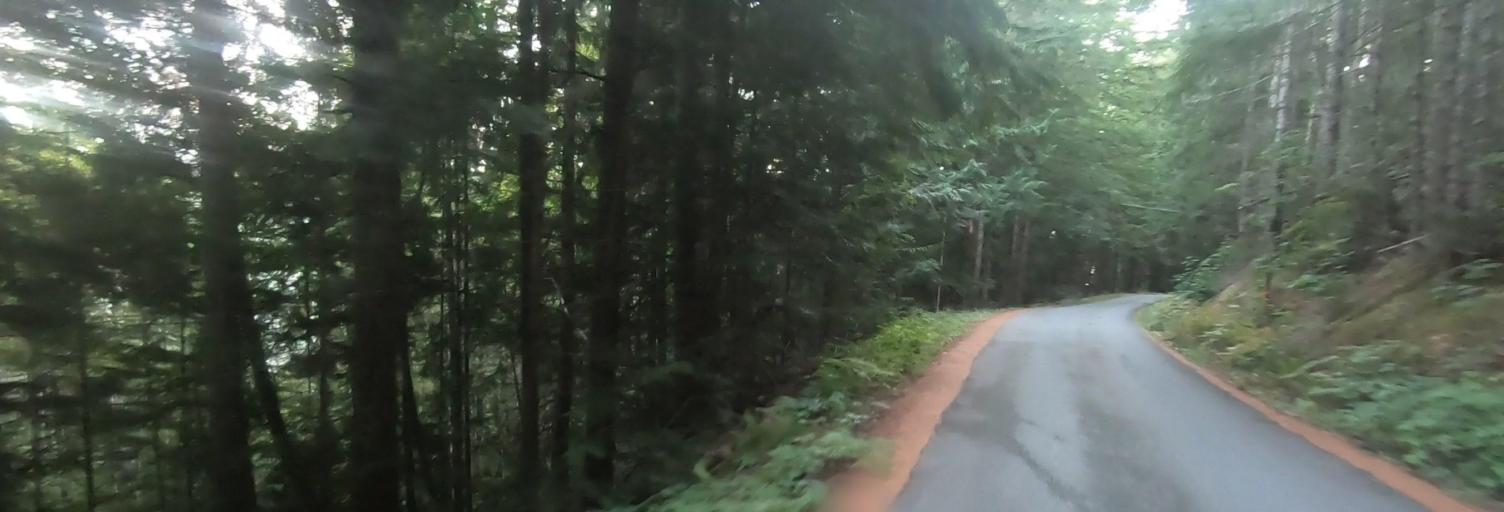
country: US
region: Washington
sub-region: Whatcom County
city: Peaceful Valley
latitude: 48.9043
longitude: -121.9420
